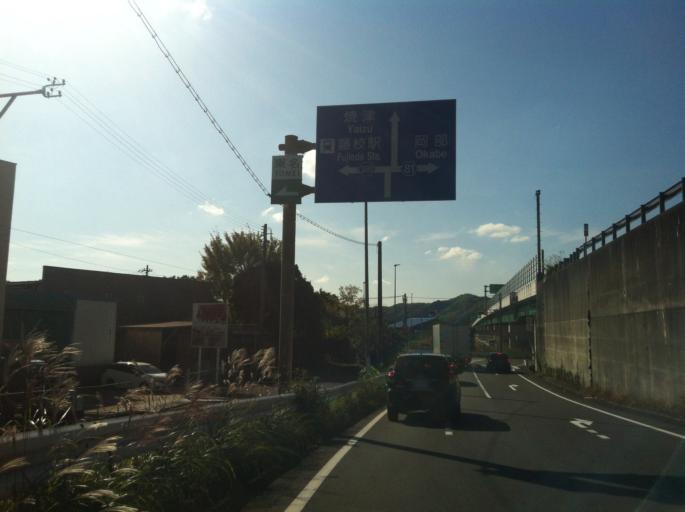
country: JP
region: Shizuoka
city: Fujieda
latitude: 34.9028
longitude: 138.2853
